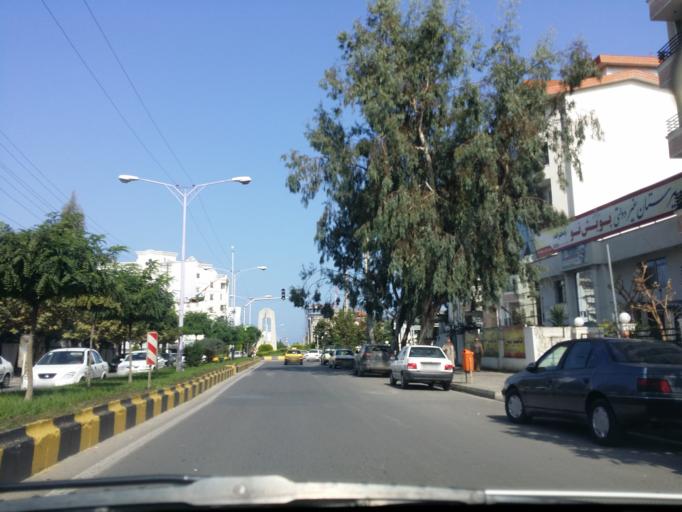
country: IR
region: Mazandaran
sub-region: Nowshahr
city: Nowshahr
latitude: 36.6467
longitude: 51.4927
